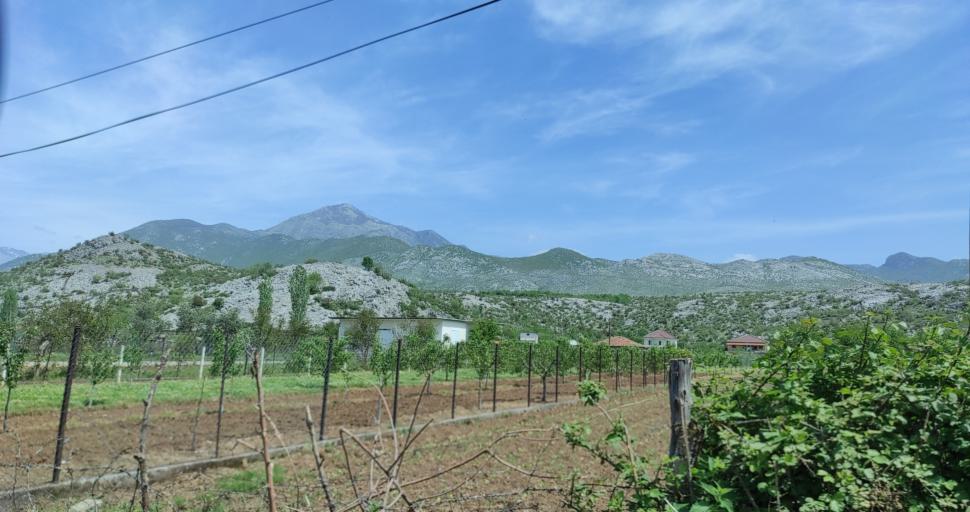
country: AL
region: Shkoder
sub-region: Rrethi i Malesia e Madhe
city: Gruemire
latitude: 42.1315
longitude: 19.5505
